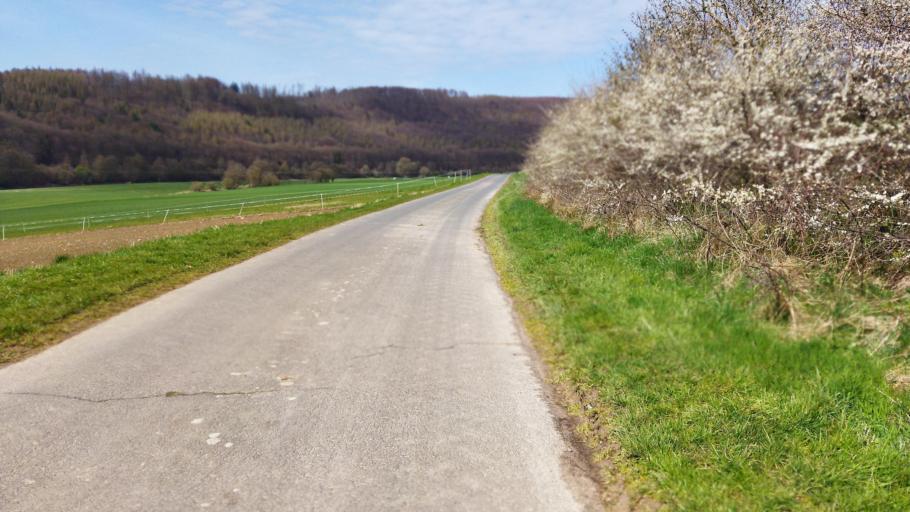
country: DE
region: Lower Saxony
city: Bad Karlshafen
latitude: 51.6317
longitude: 9.5040
